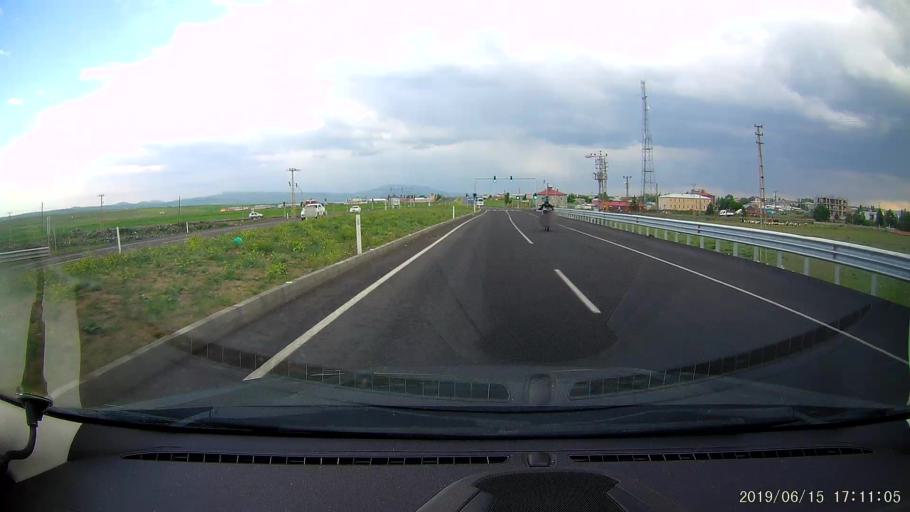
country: TR
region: Kars
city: Kars
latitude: 40.6147
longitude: 43.1333
